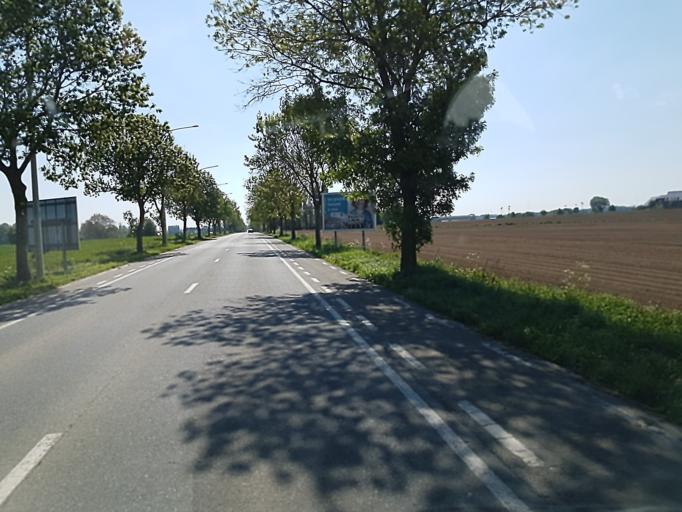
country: BE
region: Wallonia
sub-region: Province du Hainaut
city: Brugelette
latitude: 50.5911
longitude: 3.8376
